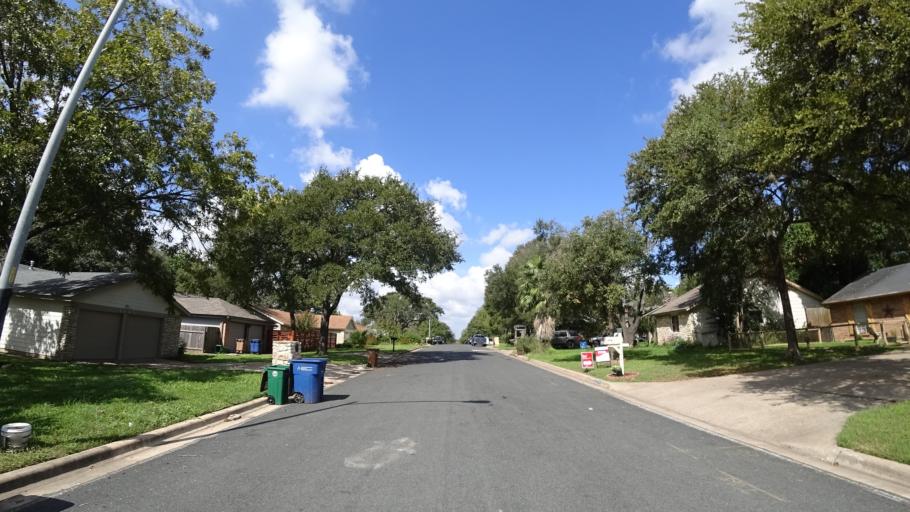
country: US
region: Texas
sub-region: Travis County
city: Onion Creek
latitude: 30.1970
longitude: -97.7943
